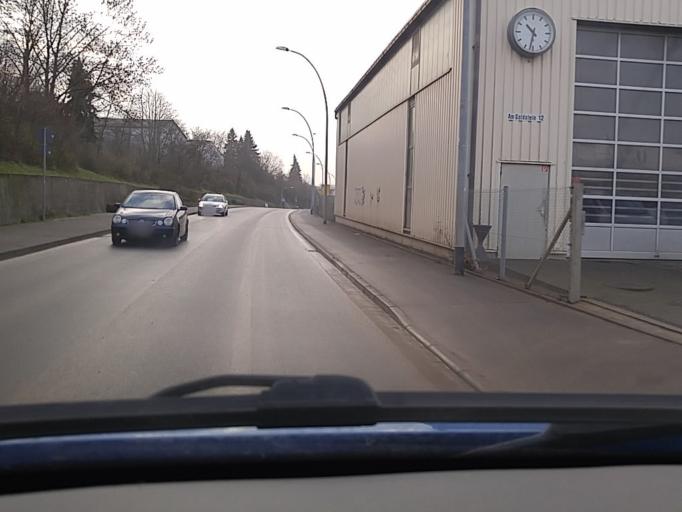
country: DE
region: Hesse
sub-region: Regierungsbezirk Darmstadt
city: Bad Nauheim
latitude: 50.3653
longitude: 8.7508
